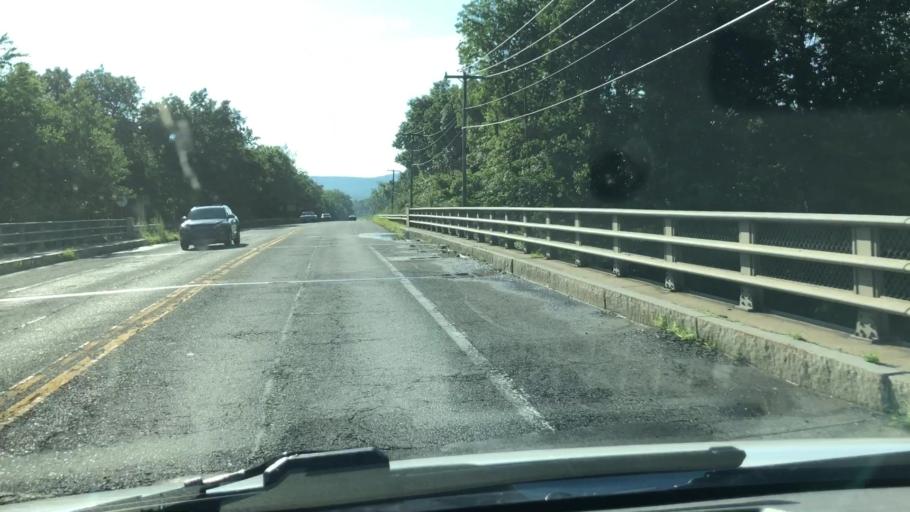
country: US
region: Massachusetts
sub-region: Franklin County
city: South Deerfield
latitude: 42.4688
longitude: -72.6123
